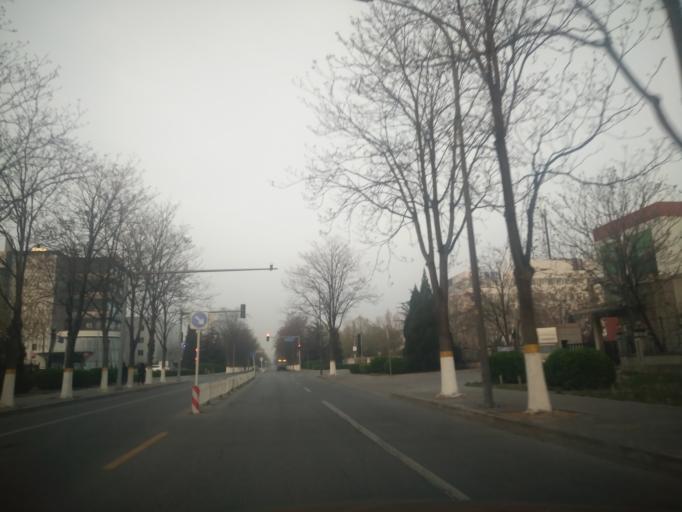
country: CN
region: Beijing
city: Jiugong
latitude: 39.8036
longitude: 116.5102
